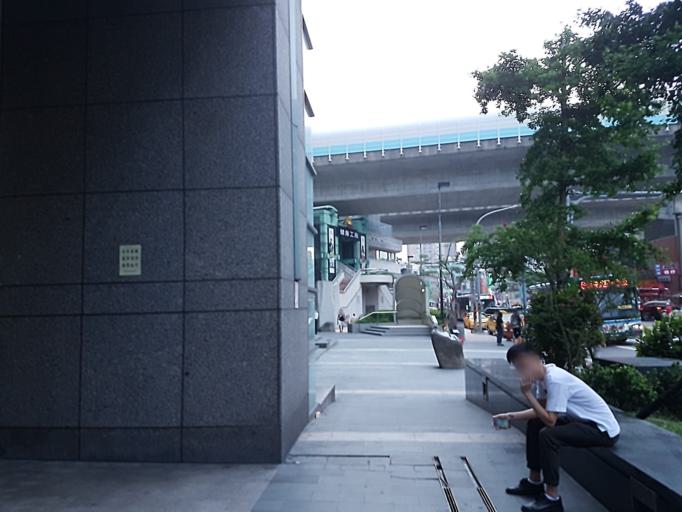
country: TW
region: Taipei
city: Taipei
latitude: 24.9577
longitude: 121.5380
